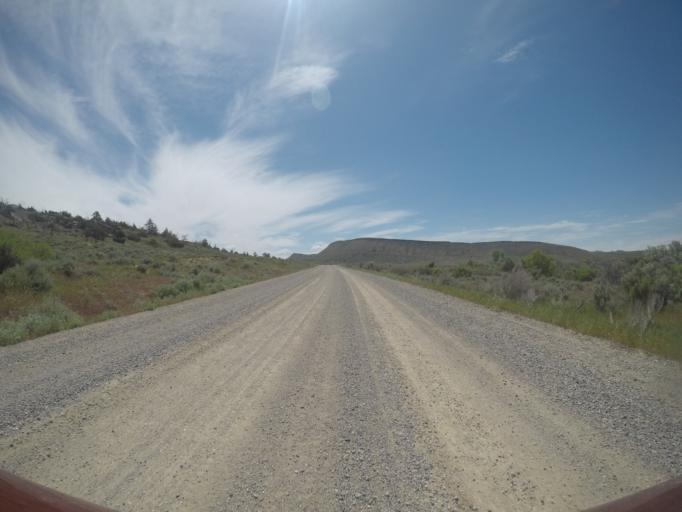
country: US
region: Montana
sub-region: Carbon County
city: Red Lodge
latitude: 45.2143
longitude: -108.8416
